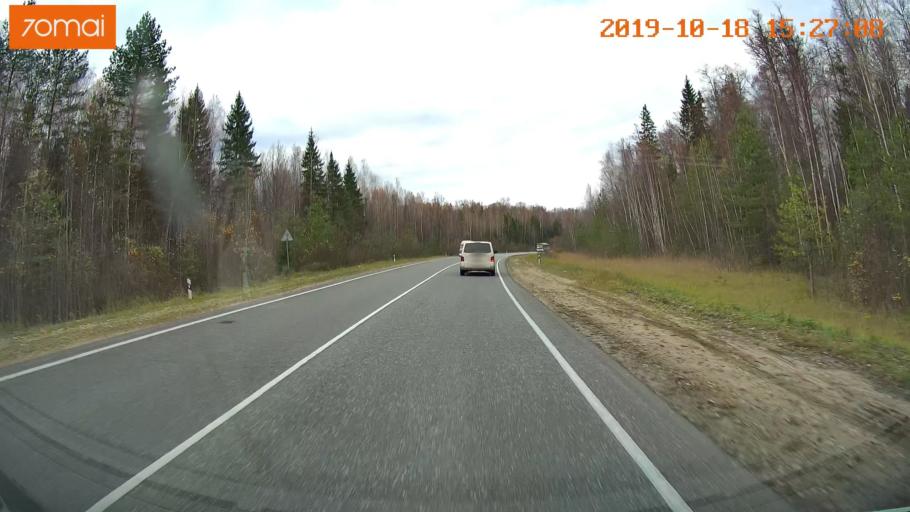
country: RU
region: Vladimir
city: Anopino
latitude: 55.7495
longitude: 40.6726
